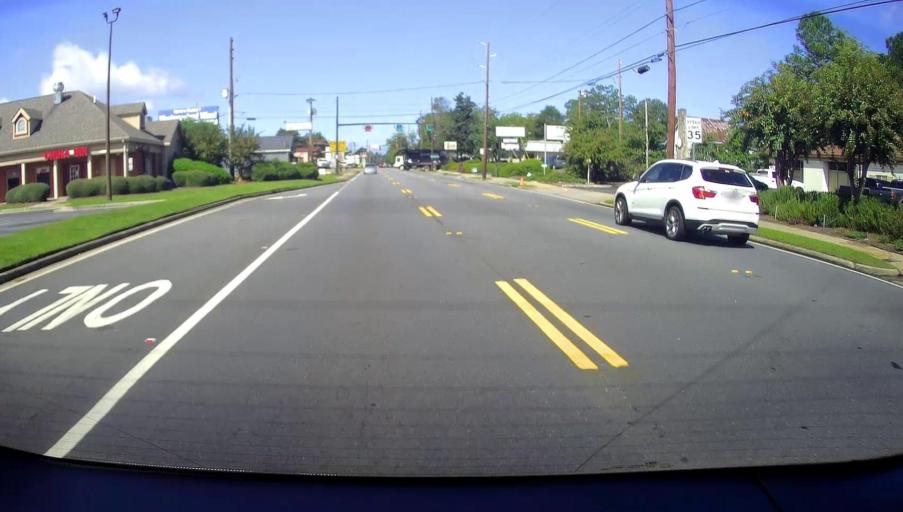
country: US
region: Georgia
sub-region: Bibb County
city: Macon
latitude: 32.8533
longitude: -83.6777
